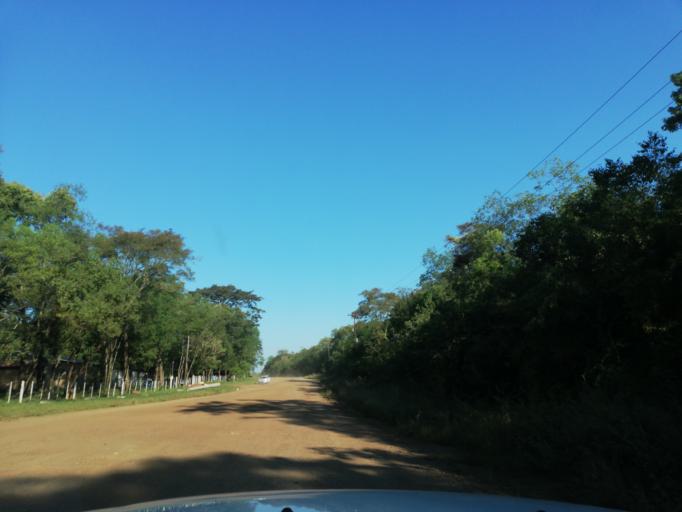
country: AR
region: Misiones
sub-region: Departamento de Candelaria
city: Candelaria
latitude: -27.5497
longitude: -55.7110
